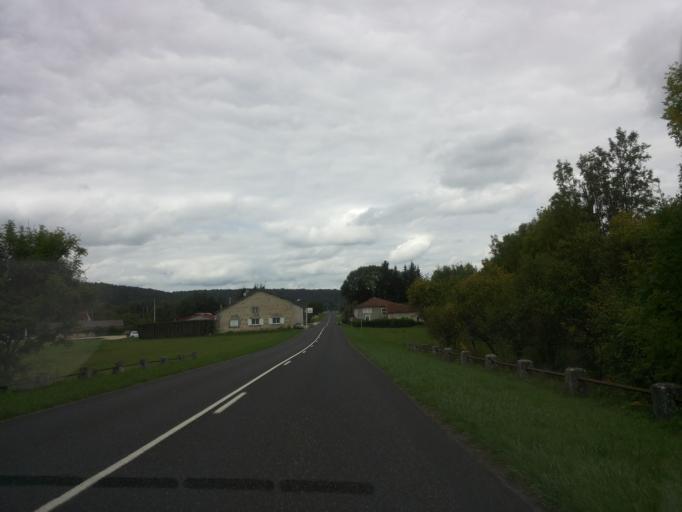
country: FR
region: Lorraine
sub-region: Departement de la Meuse
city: Ligny-en-Barrois
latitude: 48.6473
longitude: 5.3514
